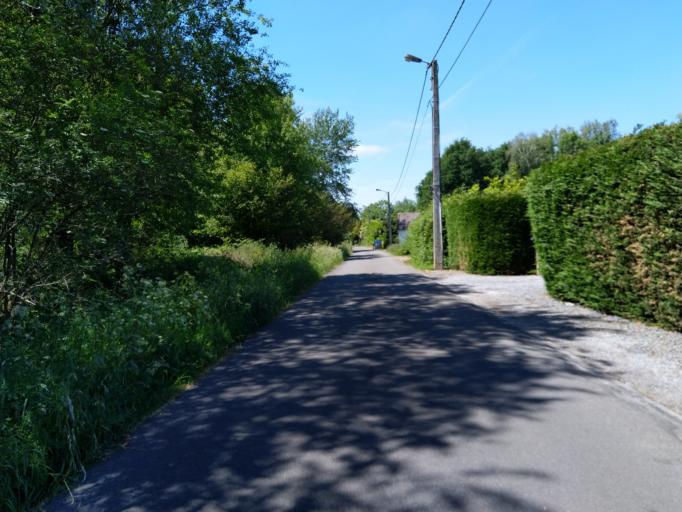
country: BE
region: Wallonia
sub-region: Province du Hainaut
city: Jurbise
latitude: 50.5075
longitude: 3.8479
